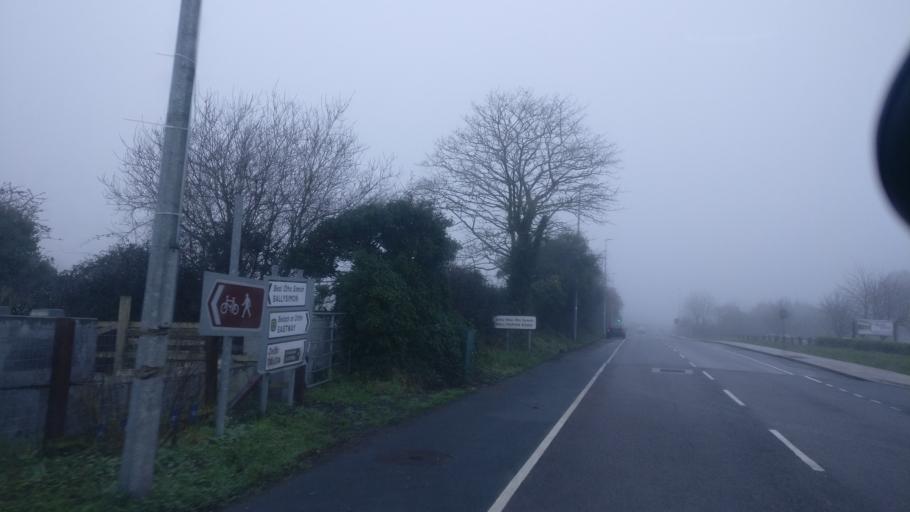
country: IE
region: Munster
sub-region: County Limerick
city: Annacotty
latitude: 52.6484
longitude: -8.5781
